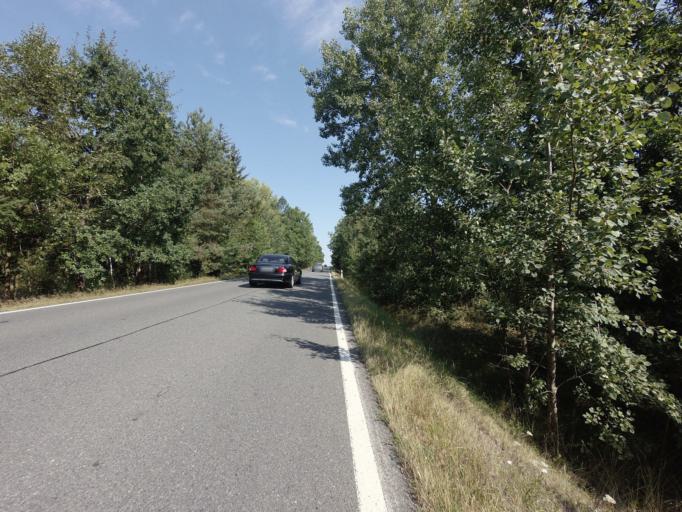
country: CZ
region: Jihocesky
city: Milevsko
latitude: 49.4238
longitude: 14.3591
